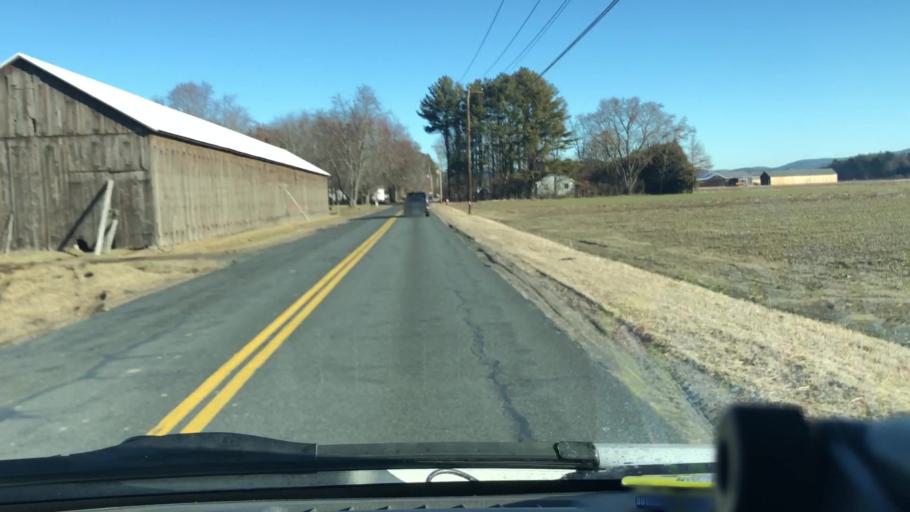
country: US
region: Massachusetts
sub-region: Hampshire County
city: North Amherst
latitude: 42.3899
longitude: -72.5476
